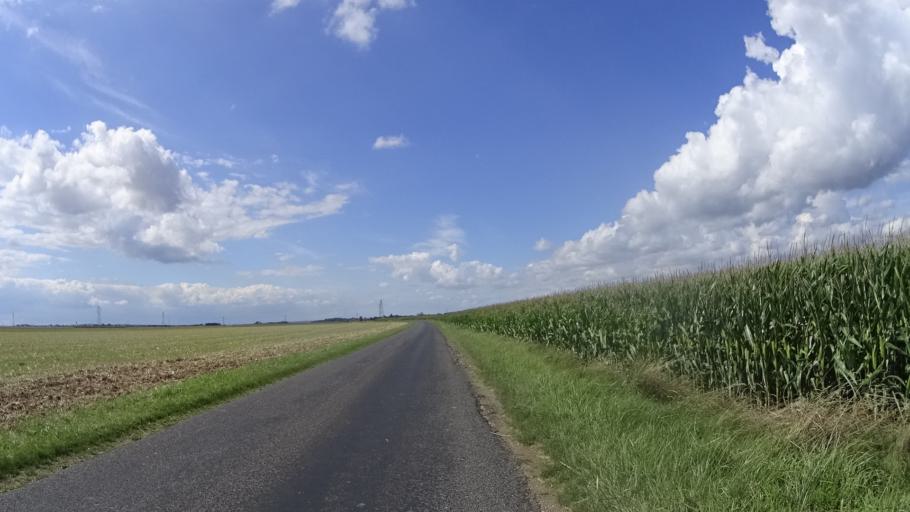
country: FR
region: Champagne-Ardenne
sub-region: Departement de la Marne
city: Pargny-sur-Saulx
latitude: 48.7042
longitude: 4.7946
